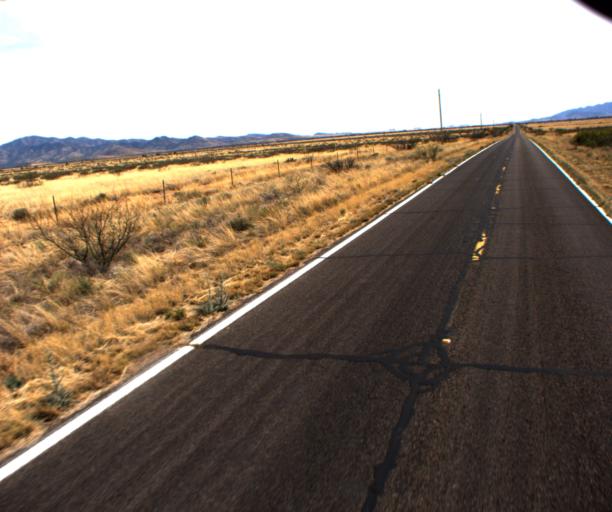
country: US
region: Arizona
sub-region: Cochise County
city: Willcox
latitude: 31.9238
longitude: -109.4914
